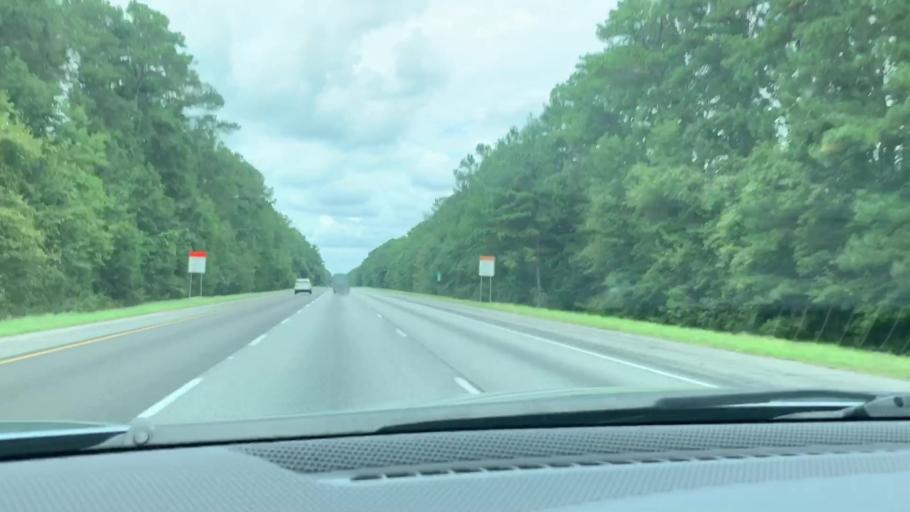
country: US
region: Georgia
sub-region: Bryan County
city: Richmond Hill
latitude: 31.8818
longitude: -81.3289
